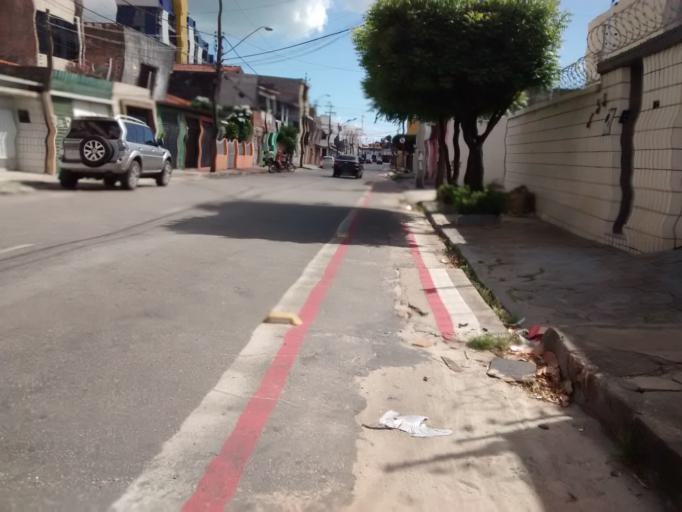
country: BR
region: Ceara
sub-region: Fortaleza
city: Fortaleza
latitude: -3.7350
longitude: -38.5506
